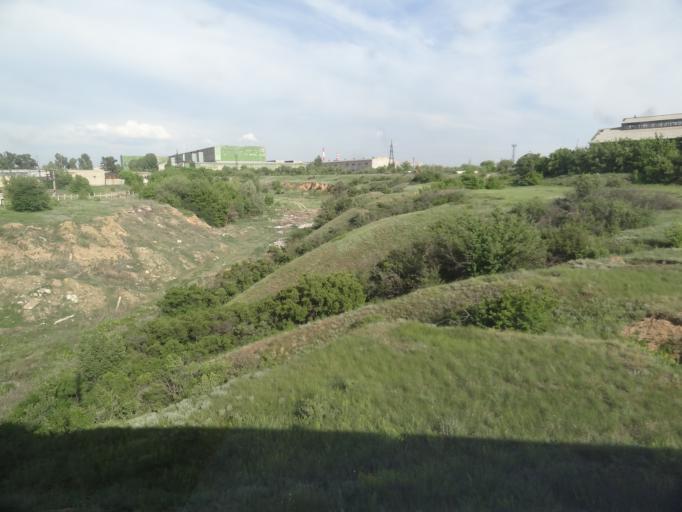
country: RU
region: Volgograd
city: Gumrak
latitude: 48.7626
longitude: 44.4344
